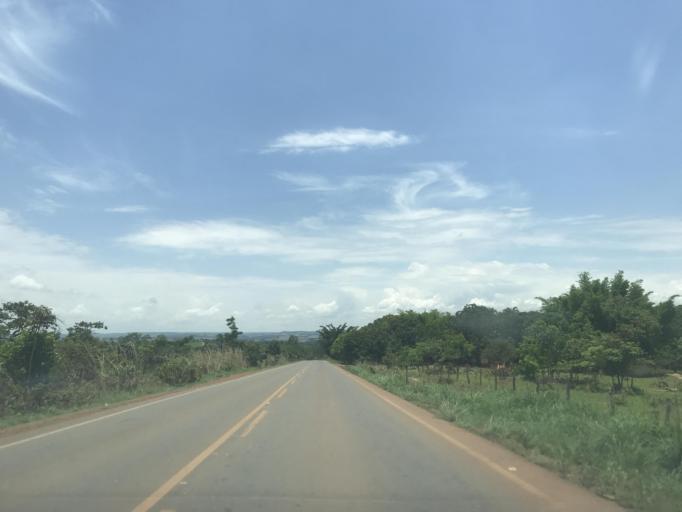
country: BR
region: Goias
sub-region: Vianopolis
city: Vianopolis
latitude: -16.5959
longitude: -48.3474
